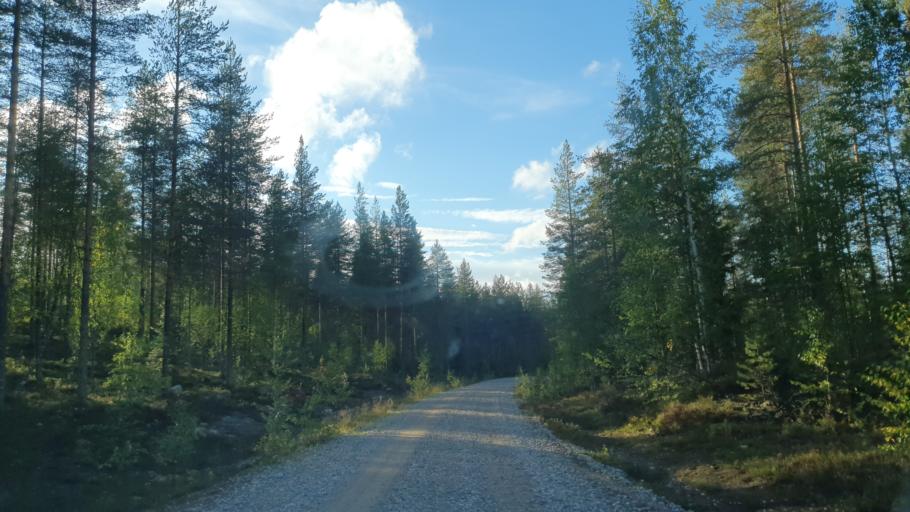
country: FI
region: Kainuu
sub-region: Kehys-Kainuu
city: Kuhmo
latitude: 64.3377
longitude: 29.9872
